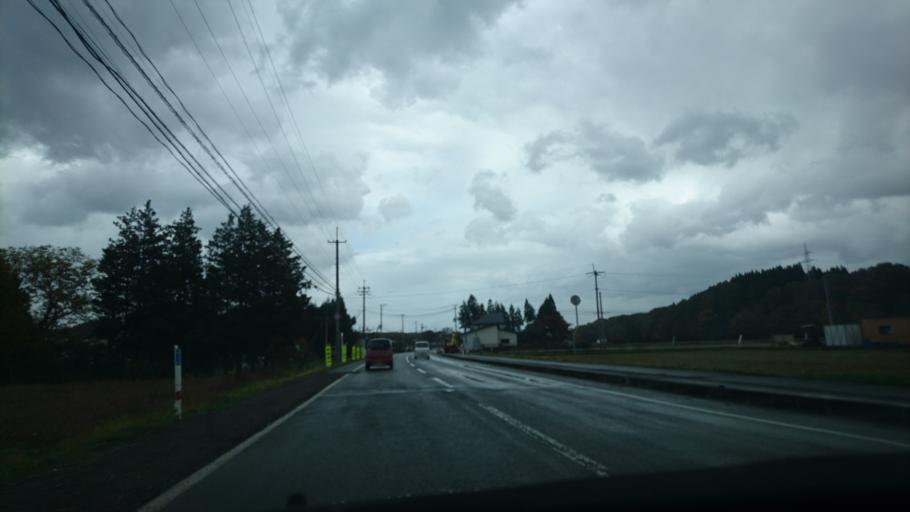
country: JP
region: Iwate
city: Shizukuishi
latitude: 39.6597
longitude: 140.9632
